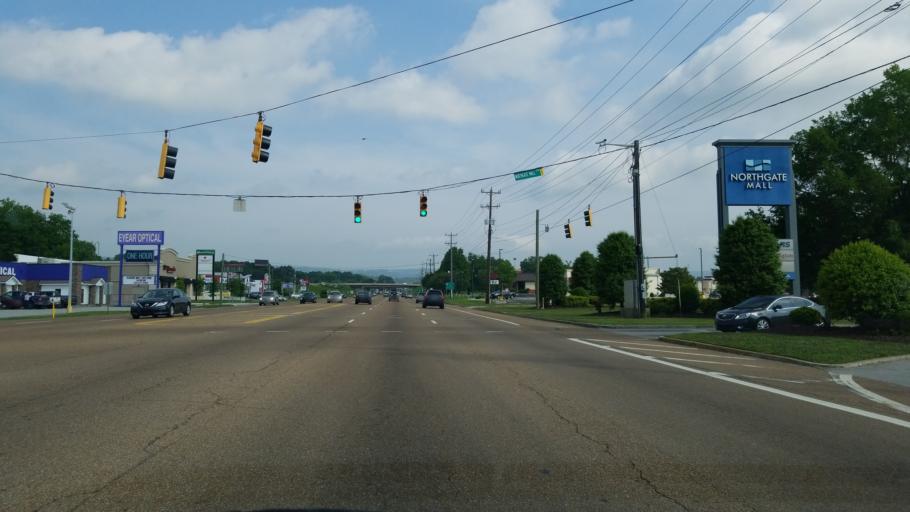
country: US
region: Tennessee
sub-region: Hamilton County
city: Red Bank
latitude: 35.1269
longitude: -85.2418
